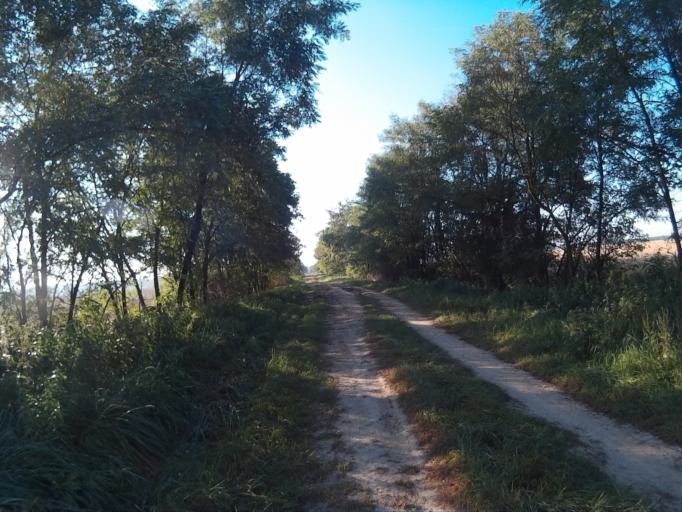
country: HU
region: Vas
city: Jak
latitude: 47.1283
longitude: 16.5872
